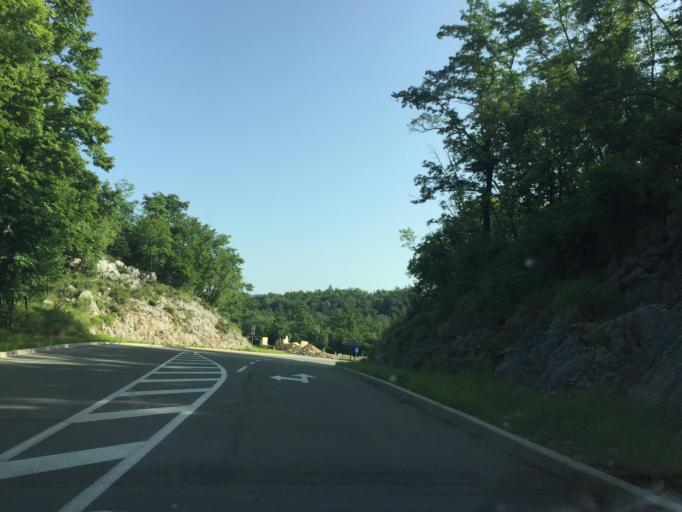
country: HR
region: Primorsko-Goranska
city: Kastav
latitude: 45.4212
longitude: 14.3229
